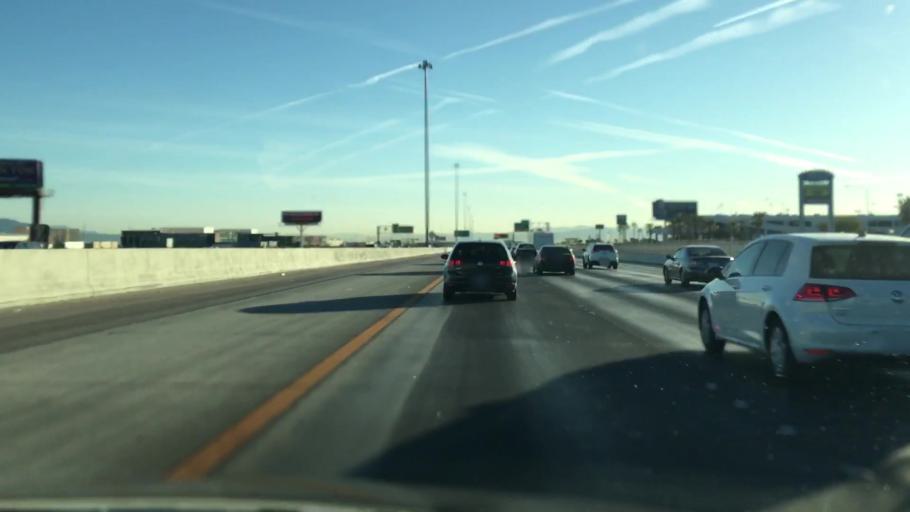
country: US
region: Nevada
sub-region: Clark County
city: Enterprise
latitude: 36.0666
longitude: -115.2382
